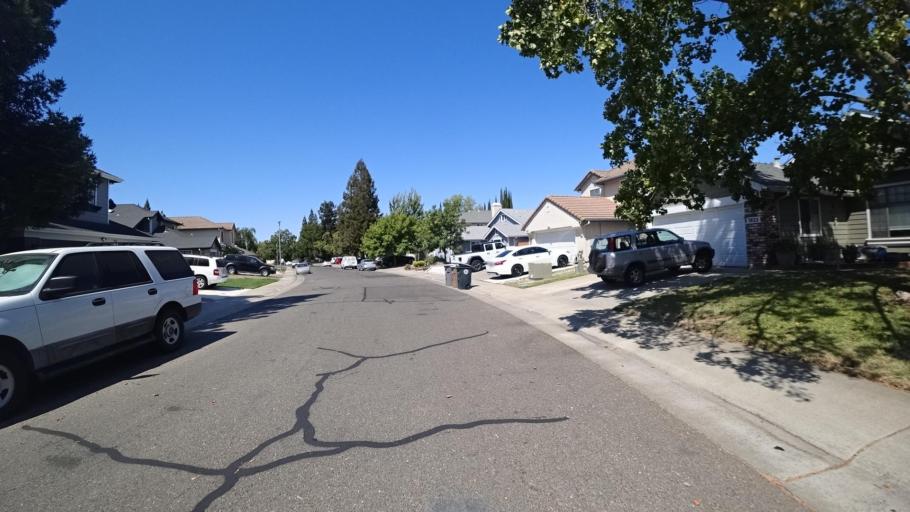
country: US
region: California
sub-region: Sacramento County
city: Laguna
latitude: 38.4174
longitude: -121.4137
